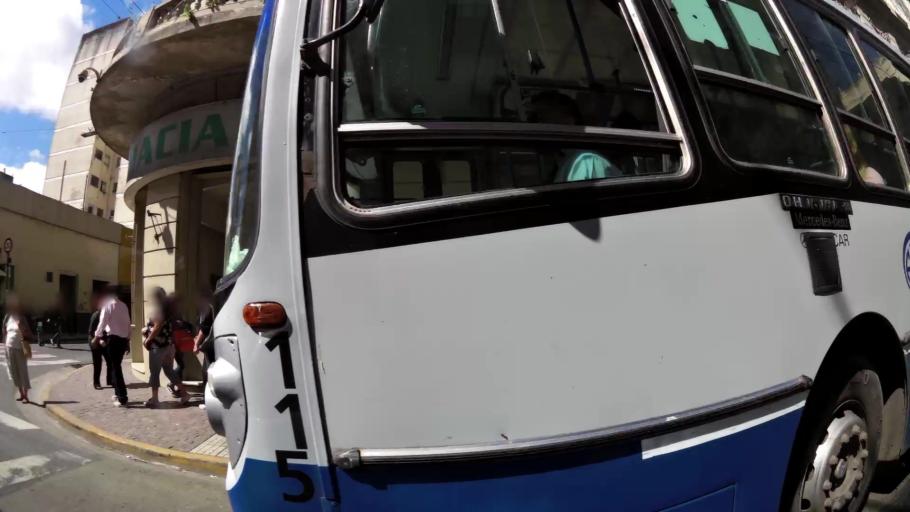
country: AR
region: Santa Fe
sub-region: Departamento de Rosario
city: Rosario
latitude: -32.9436
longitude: -60.6405
